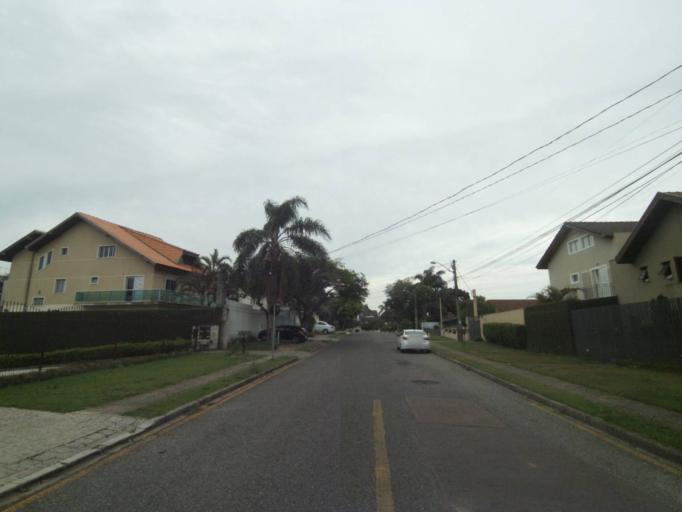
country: BR
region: Parana
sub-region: Curitiba
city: Curitiba
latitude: -25.4032
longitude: -49.2770
